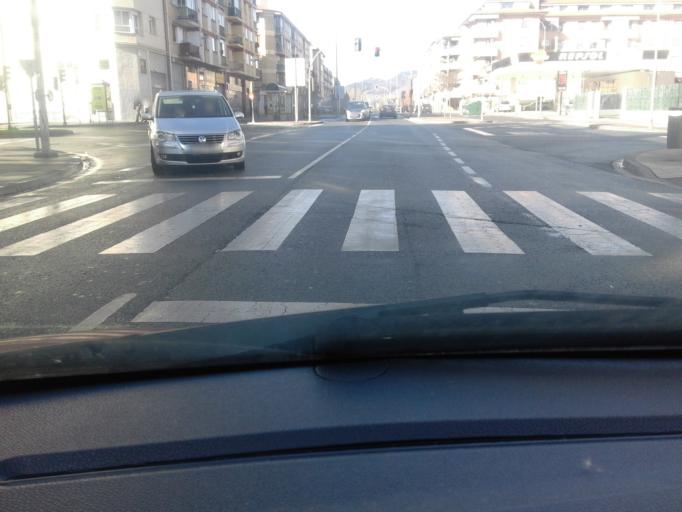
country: ES
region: Navarre
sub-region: Provincia de Navarra
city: Berriozar
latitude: 42.8361
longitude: -1.6723
